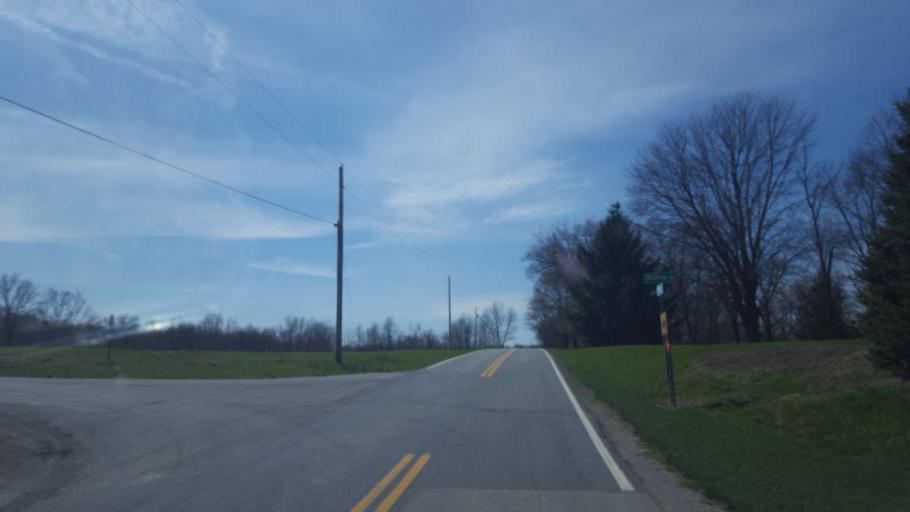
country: US
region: Ohio
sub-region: Delaware County
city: Ashley
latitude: 40.4002
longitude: -83.0331
